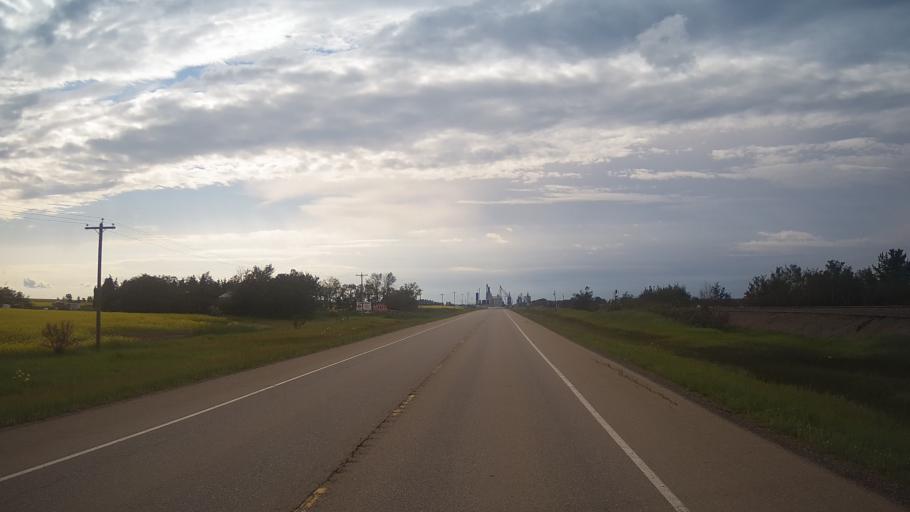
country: CA
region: Alberta
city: Viking
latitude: 53.0842
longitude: -111.7516
